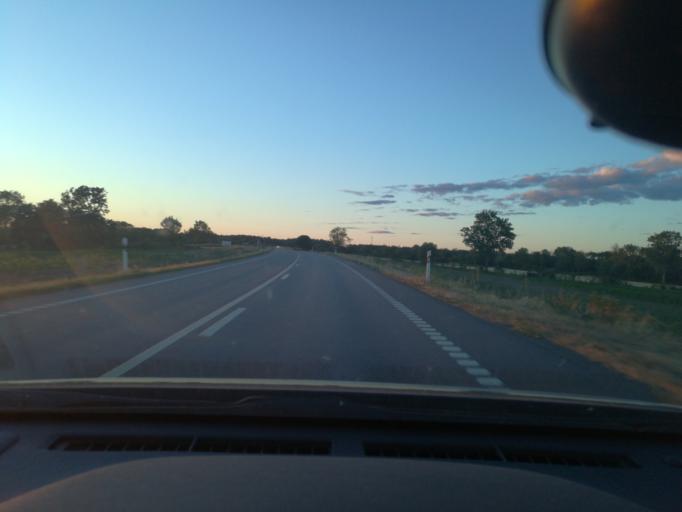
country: SE
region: Kalmar
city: Faerjestaden
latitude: 56.7370
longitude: 16.5451
